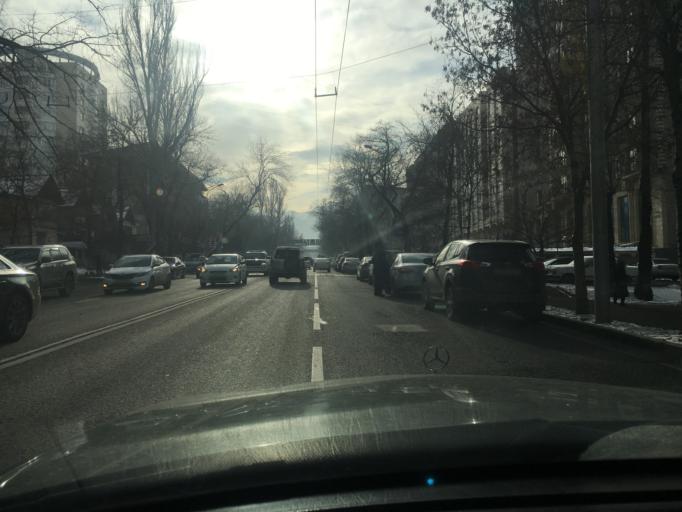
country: KZ
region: Almaty Qalasy
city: Almaty
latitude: 43.2475
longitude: 76.9336
